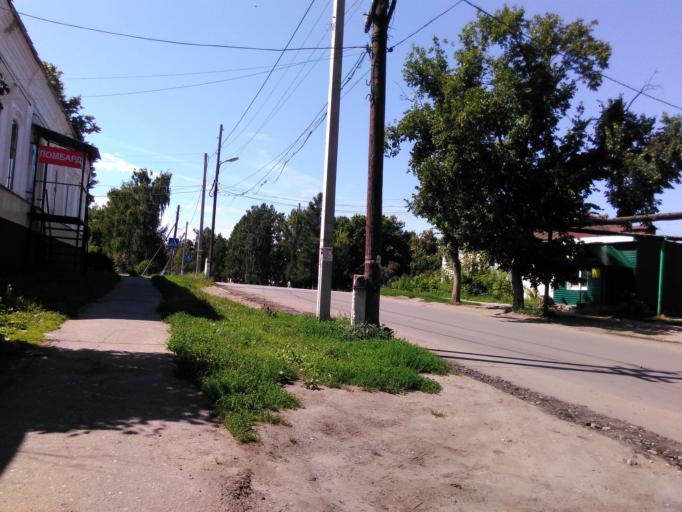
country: RU
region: Penza
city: Belinskiy
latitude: 52.9666
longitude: 43.4213
